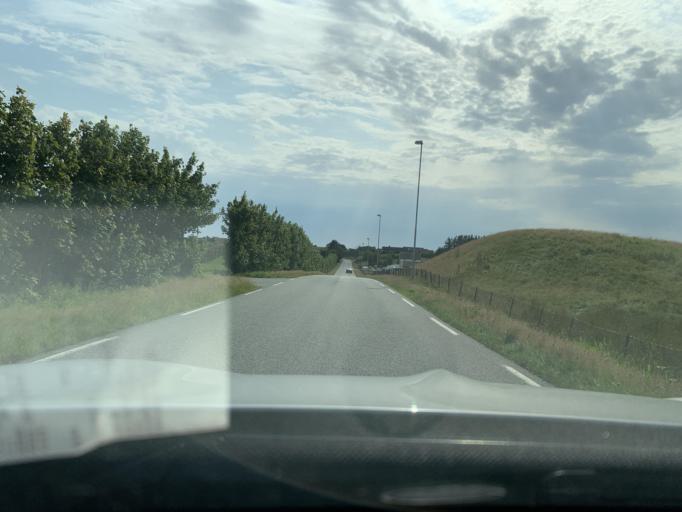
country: NO
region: Rogaland
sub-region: Time
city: Bryne
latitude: 58.7371
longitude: 5.6073
